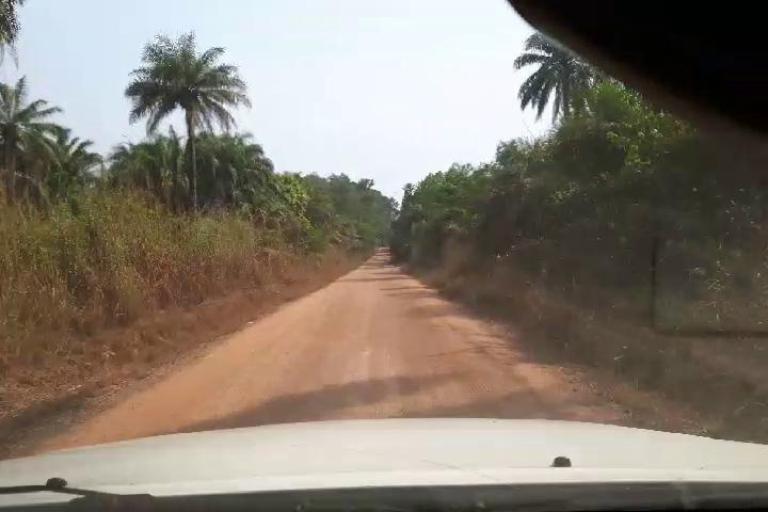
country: SL
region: Northern Province
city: Masingbi
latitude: 8.7820
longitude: -11.8730
